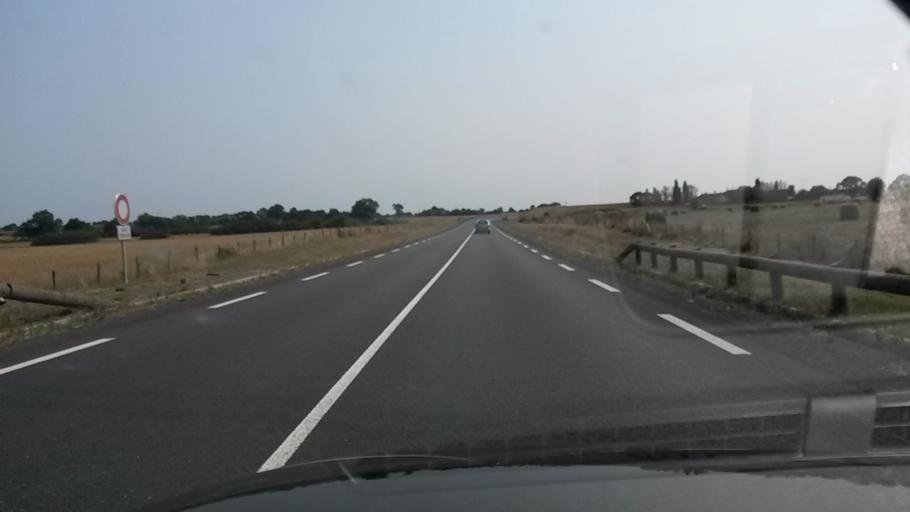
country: FR
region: Pays de la Loire
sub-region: Departement de la Loire-Atlantique
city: Mesanger
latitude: 47.4229
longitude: -1.1863
